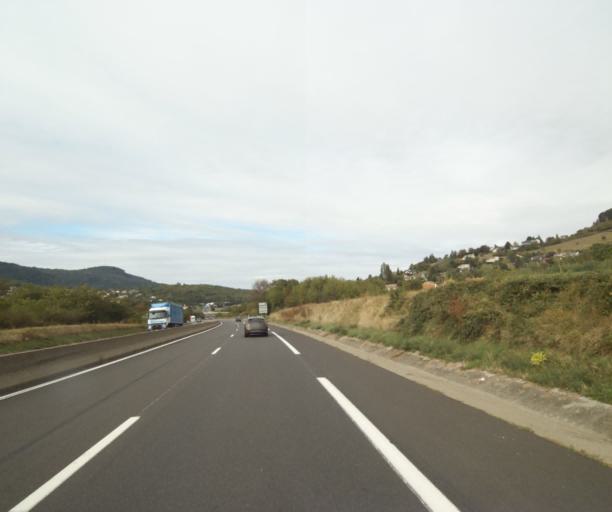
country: FR
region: Auvergne
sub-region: Departement du Puy-de-Dome
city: Ceyrat
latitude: 45.7252
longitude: 3.0718
